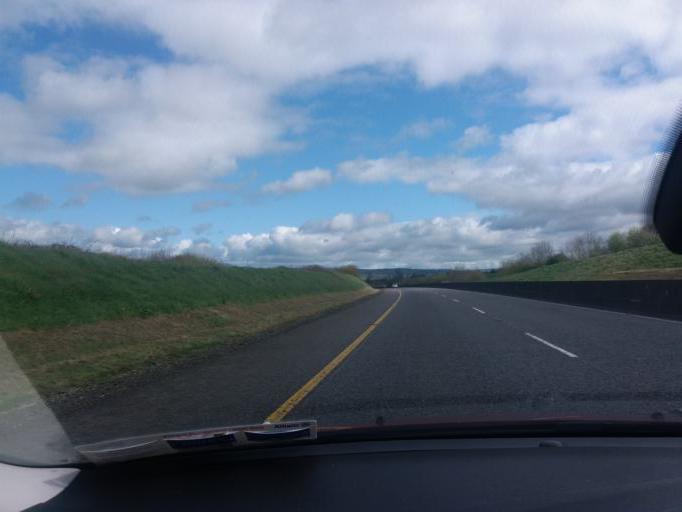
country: IE
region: Munster
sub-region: County Cork
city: Fermoy
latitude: 52.1253
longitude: -8.2629
